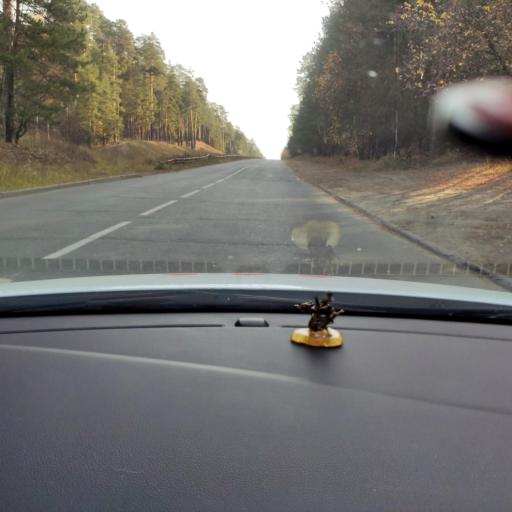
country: RU
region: Tatarstan
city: Osinovo
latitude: 55.8266
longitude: 48.8968
